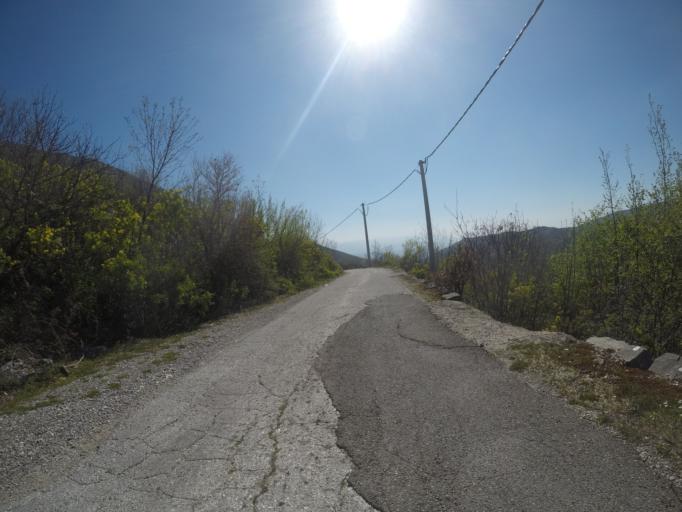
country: ME
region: Danilovgrad
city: Danilovgrad
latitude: 42.5298
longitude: 19.0278
